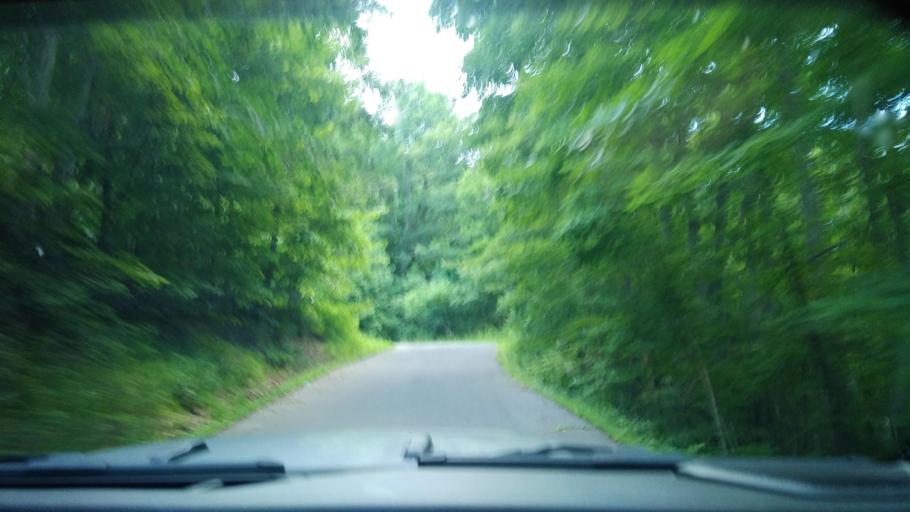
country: US
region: Tennessee
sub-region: Sevier County
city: Gatlinburg
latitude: 35.7408
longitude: -83.4824
